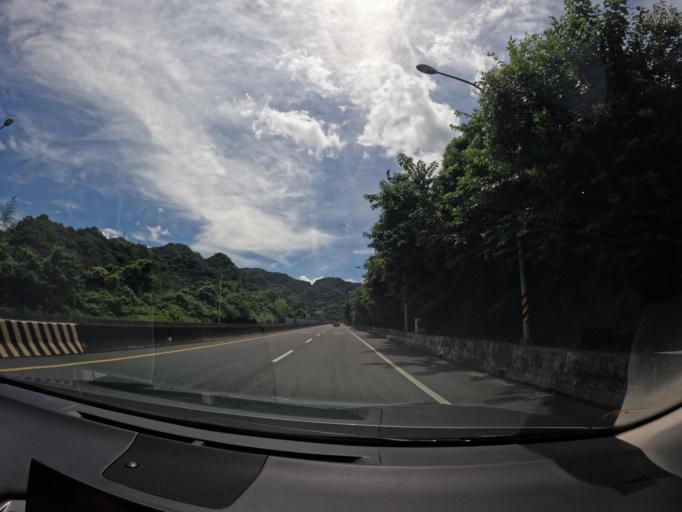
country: TW
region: Taiwan
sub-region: Miaoli
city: Miaoli
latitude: 24.4643
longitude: 120.8380
